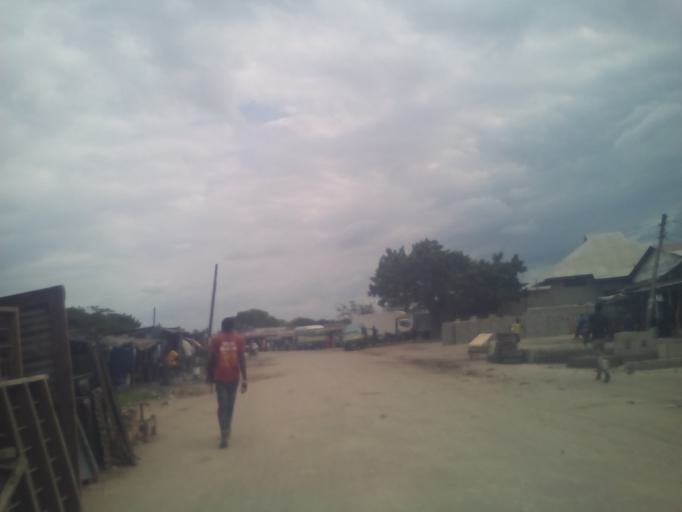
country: TZ
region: Dar es Salaam
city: Dar es Salaam
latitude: -6.8680
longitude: 39.2311
